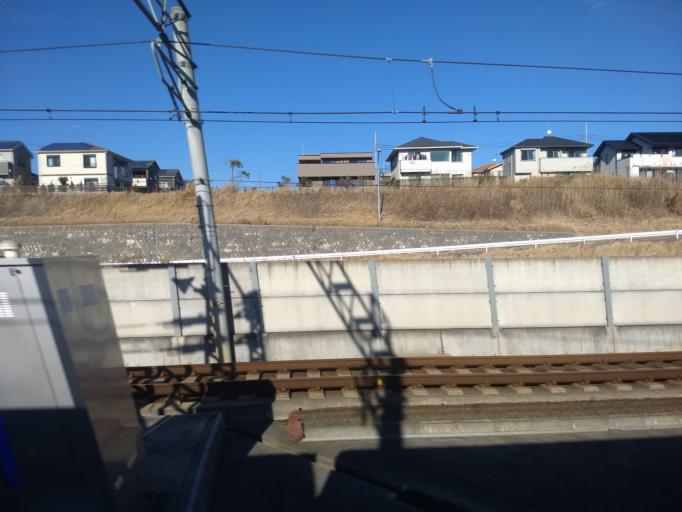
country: JP
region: Chiba
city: Sakura
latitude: 35.7864
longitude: 140.2076
